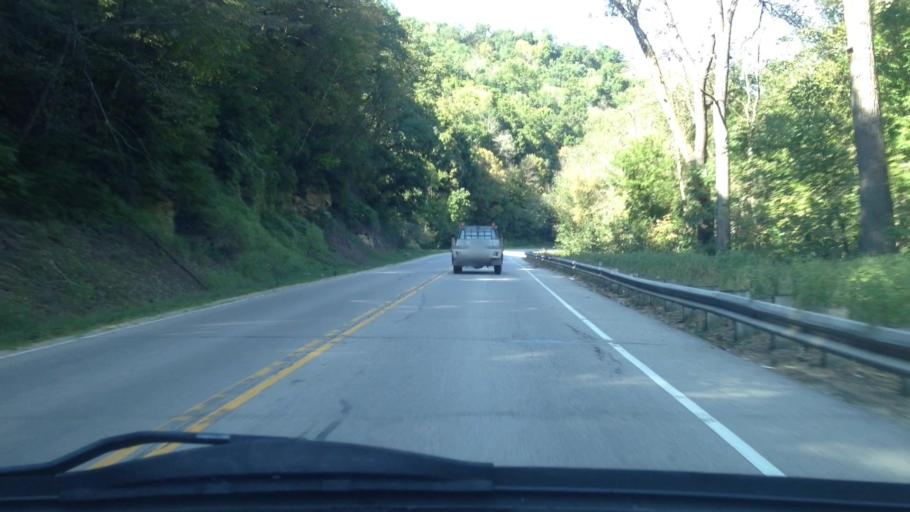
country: US
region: Minnesota
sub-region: Fillmore County
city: Rushford
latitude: 43.7602
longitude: -91.7655
